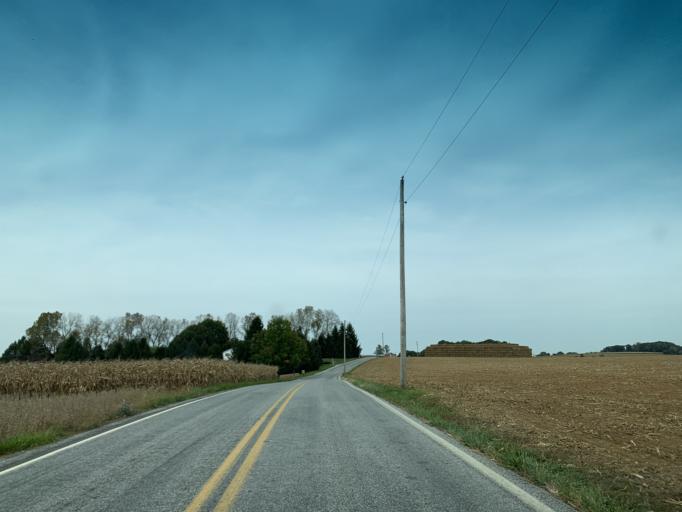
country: US
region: Pennsylvania
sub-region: York County
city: Windsor
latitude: 39.8588
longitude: -76.5144
